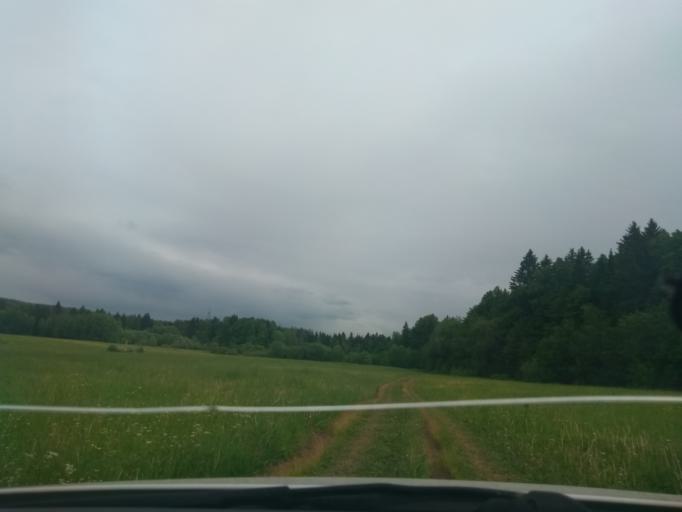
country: RU
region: Perm
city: Ferma
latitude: 57.9802
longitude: 56.3378
